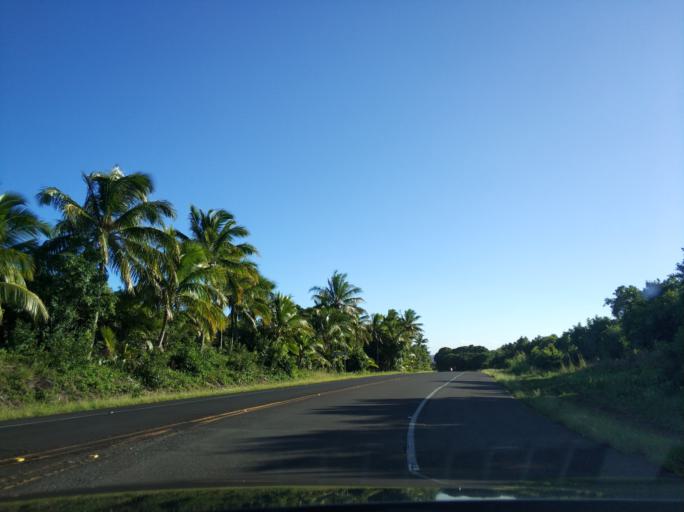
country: US
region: Hawaii
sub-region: Hawaii County
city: Leilani Estates
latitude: 19.3674
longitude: -154.9657
